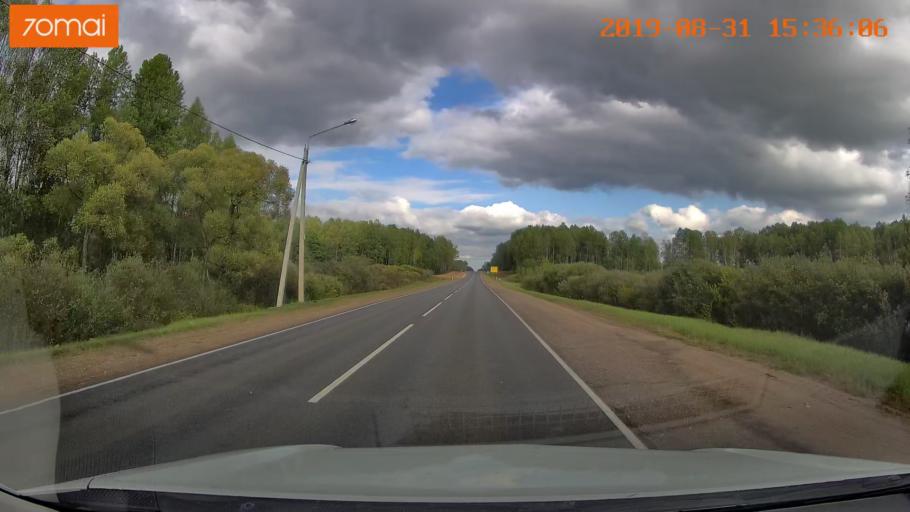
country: RU
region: Kaluga
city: Mosal'sk
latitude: 54.6089
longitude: 34.7505
